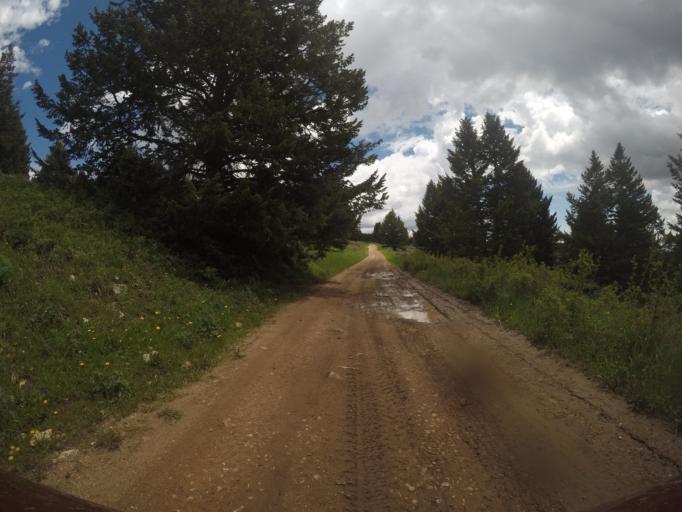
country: US
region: Wyoming
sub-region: Big Horn County
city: Lovell
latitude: 45.1711
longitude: -108.4304
